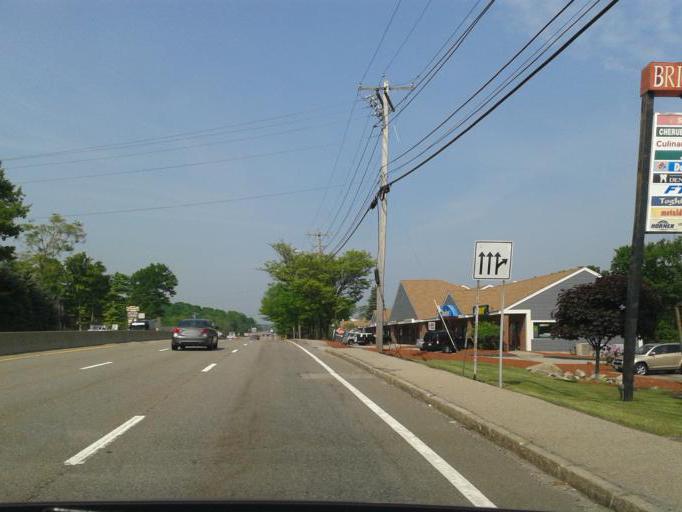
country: US
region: Massachusetts
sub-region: Worcester County
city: Southborough
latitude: 42.2971
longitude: -71.4926
